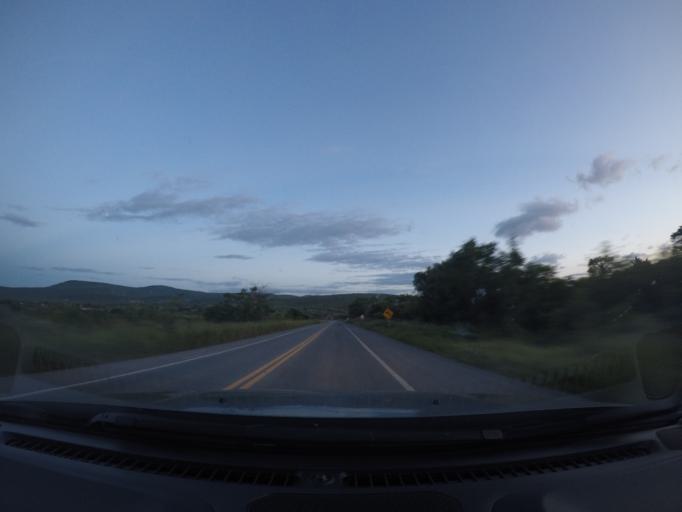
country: BR
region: Bahia
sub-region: Seabra
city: Seabra
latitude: -12.4868
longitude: -41.7345
